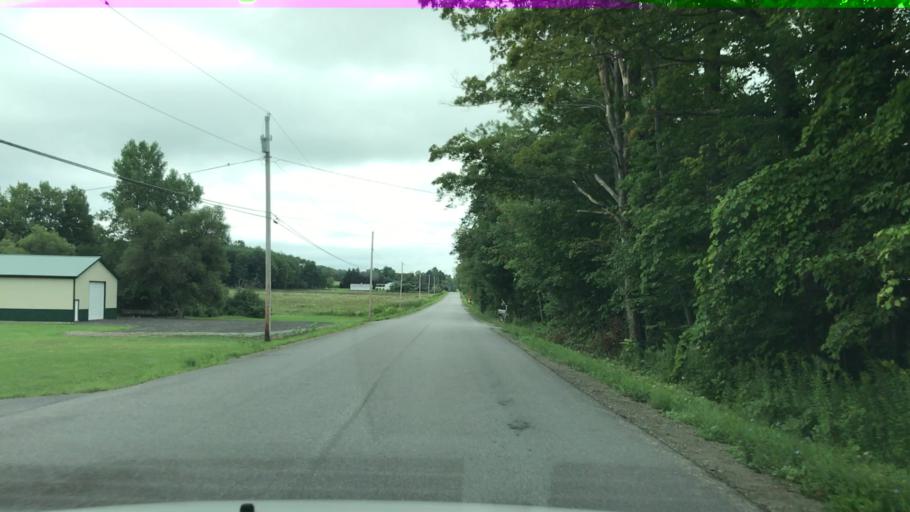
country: US
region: New York
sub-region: Wyoming County
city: Attica
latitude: 42.8285
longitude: -78.3363
